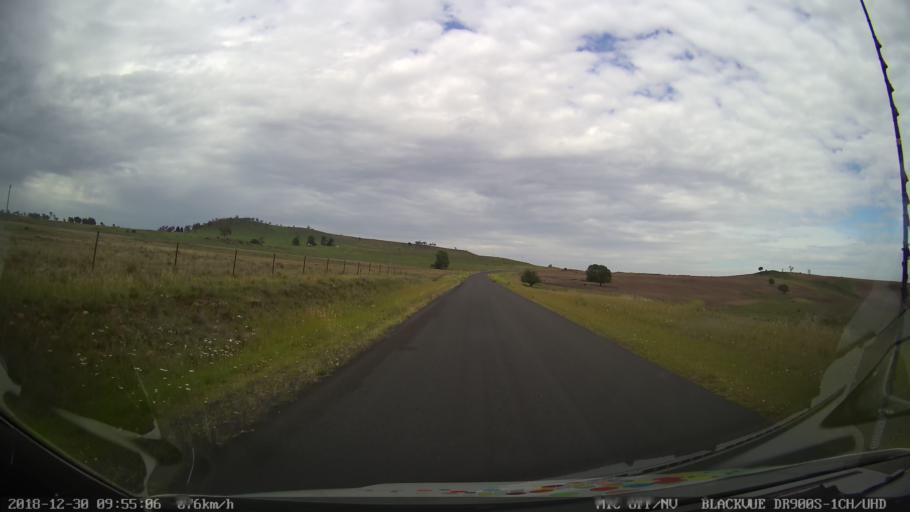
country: AU
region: New South Wales
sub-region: Cooma-Monaro
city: Cooma
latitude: -36.5195
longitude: 149.2692
